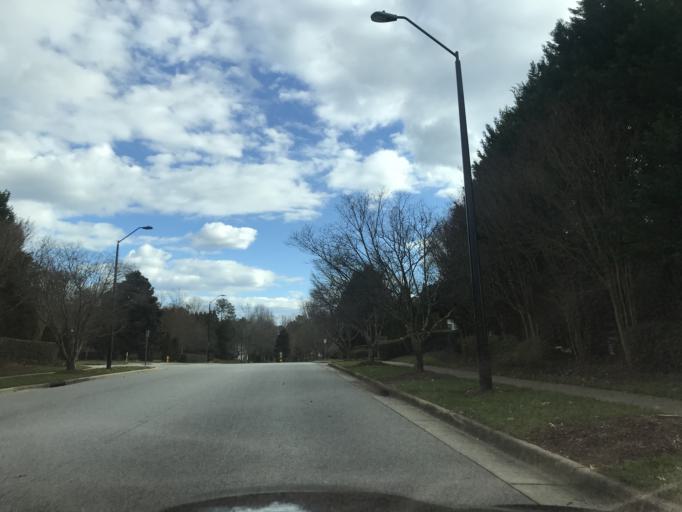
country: US
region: North Carolina
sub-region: Wake County
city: West Raleigh
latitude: 35.8602
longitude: -78.7191
